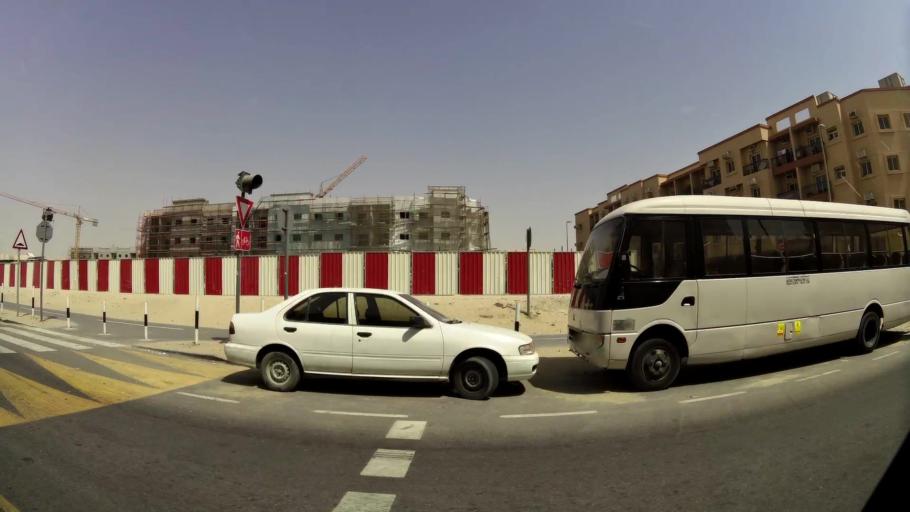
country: AE
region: Dubai
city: Dubai
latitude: 25.1517
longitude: 55.2441
